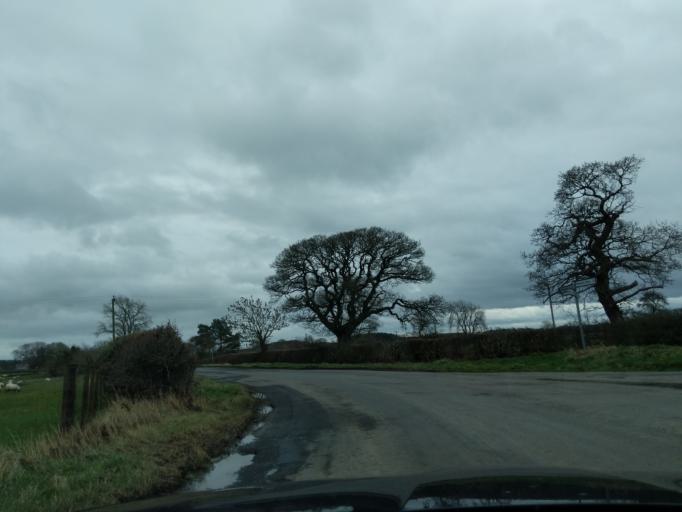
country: GB
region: England
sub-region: Northumberland
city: Morpeth
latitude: 55.1796
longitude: -1.7391
